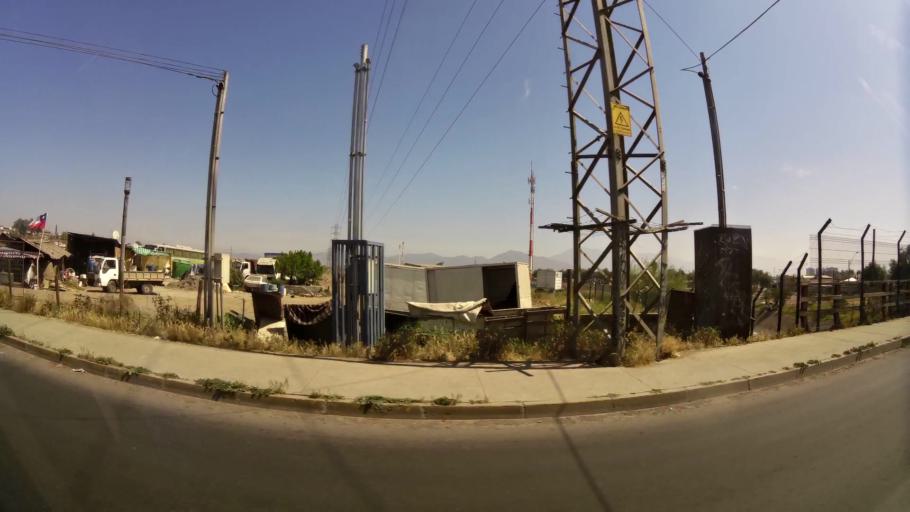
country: CL
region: Santiago Metropolitan
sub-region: Provincia de Santiago
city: Lo Prado
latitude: -33.4826
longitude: -70.7247
